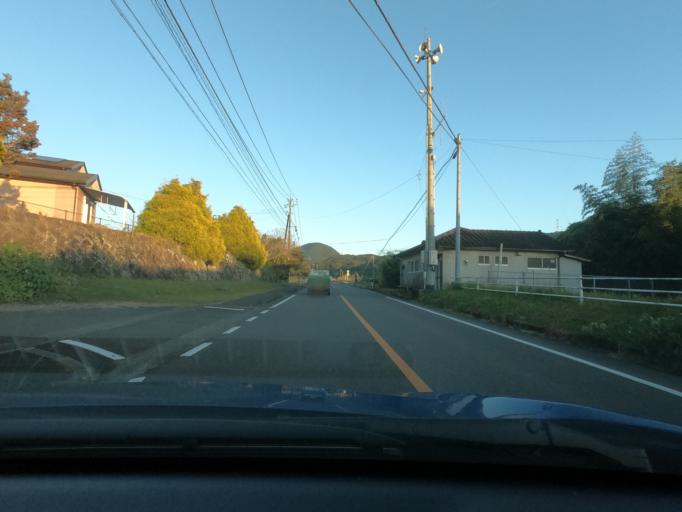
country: JP
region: Kagoshima
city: Satsumasendai
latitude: 31.7913
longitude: 130.4597
